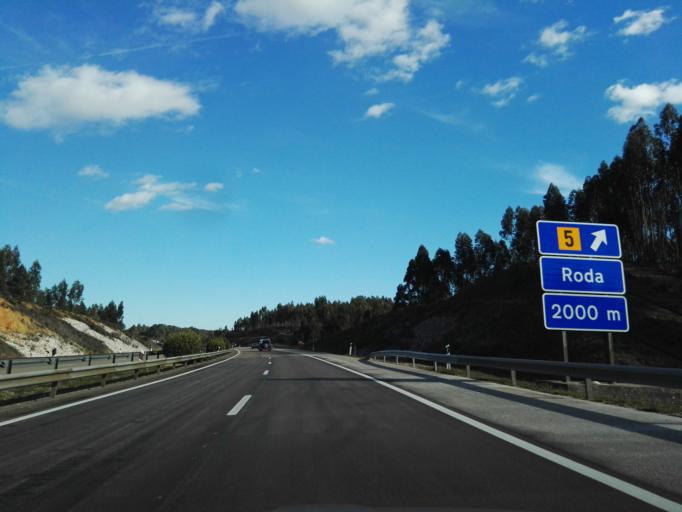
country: PT
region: Santarem
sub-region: Chamusca
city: Vila Nova da Barquinha
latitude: 39.4857
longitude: -8.4146
